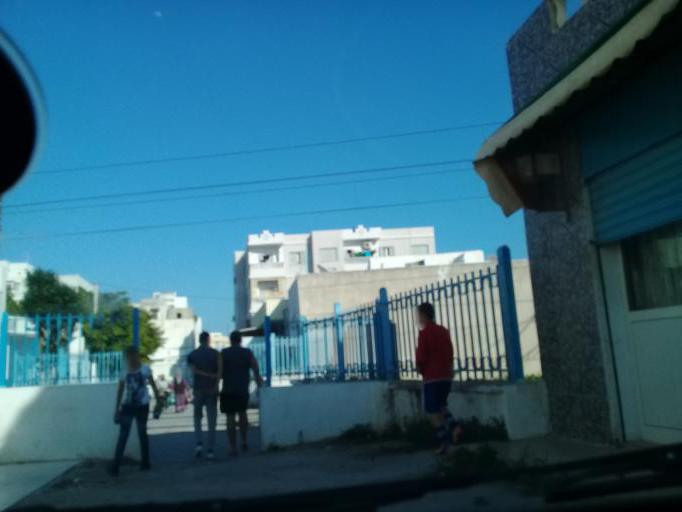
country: TN
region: Tunis
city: La Goulette
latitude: 36.8198
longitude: 10.3051
